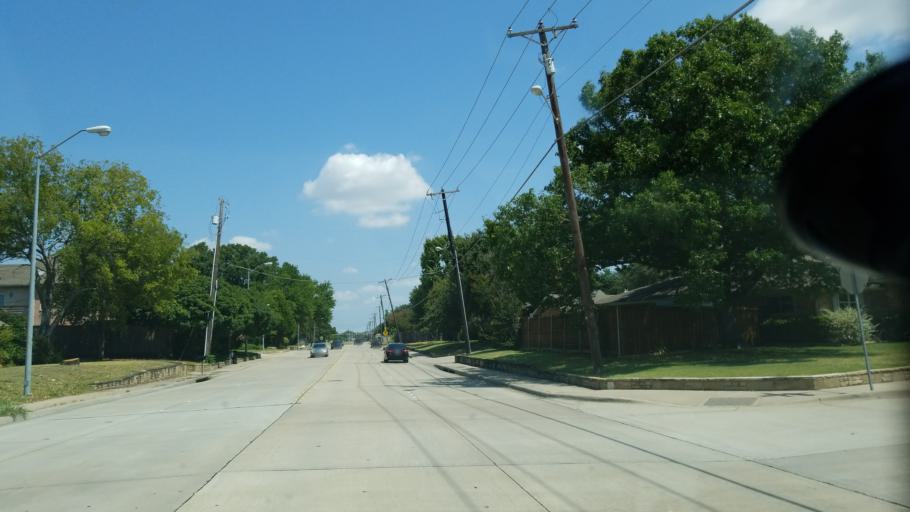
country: US
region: Texas
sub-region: Dallas County
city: Richardson
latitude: 32.9306
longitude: -96.7340
